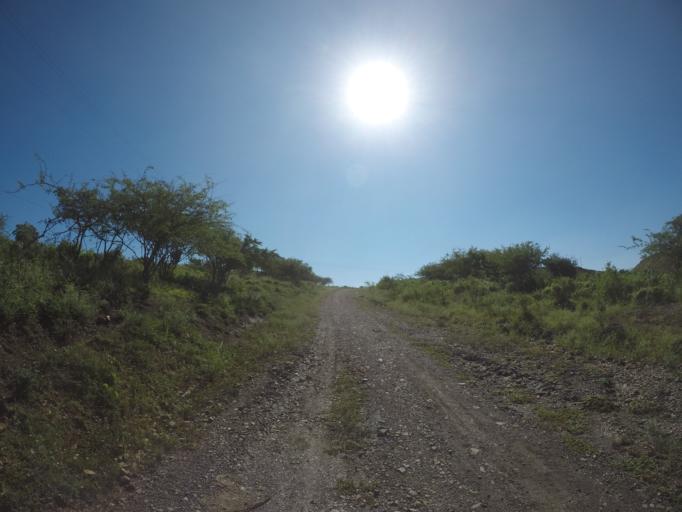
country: ZA
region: KwaZulu-Natal
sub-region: uThungulu District Municipality
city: Empangeni
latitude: -28.5709
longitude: 31.7112
